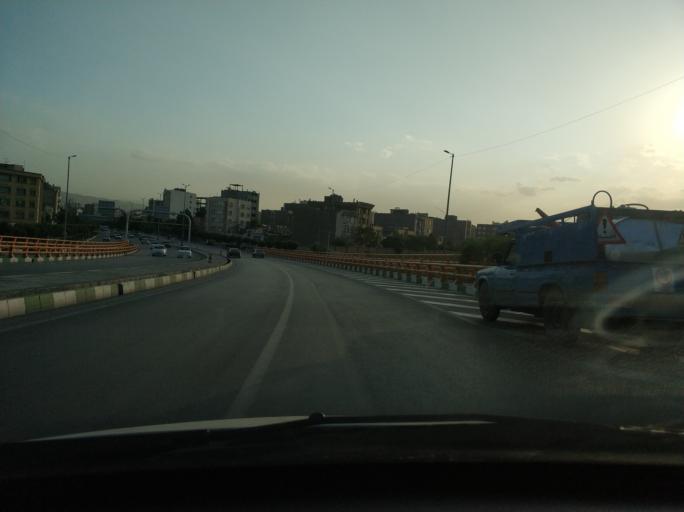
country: IR
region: Razavi Khorasan
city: Mashhad
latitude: 36.3401
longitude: 59.5451
